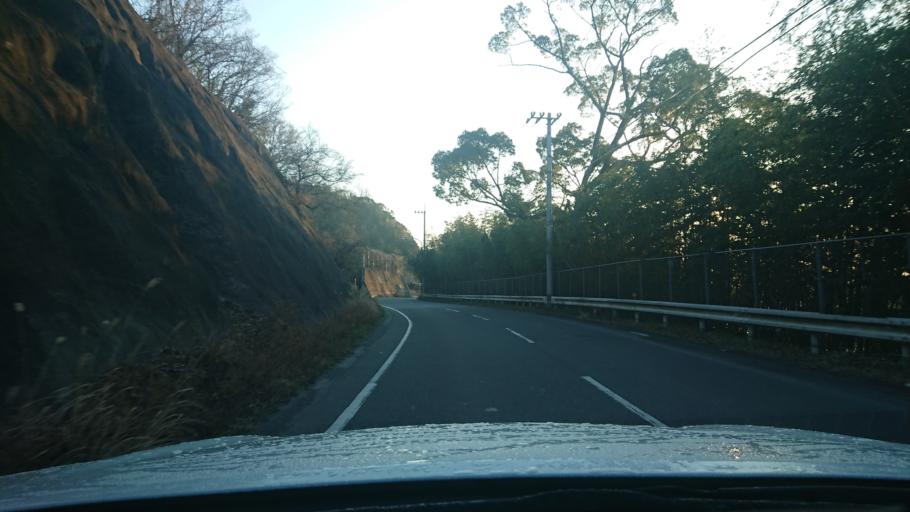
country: JP
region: Tokushima
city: Komatsushimacho
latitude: 33.9436
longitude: 134.5835
